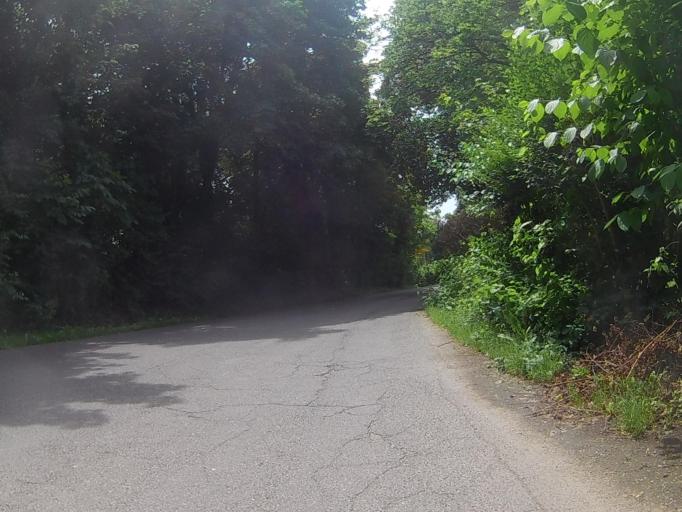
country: SI
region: Maribor
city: Maribor
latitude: 46.5683
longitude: 15.6489
